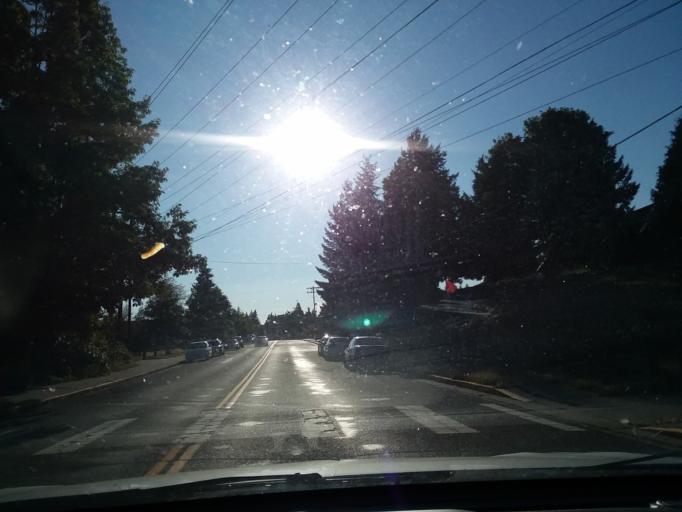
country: US
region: Washington
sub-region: Snohomish County
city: Lynnwood
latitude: 47.8033
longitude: -122.3258
